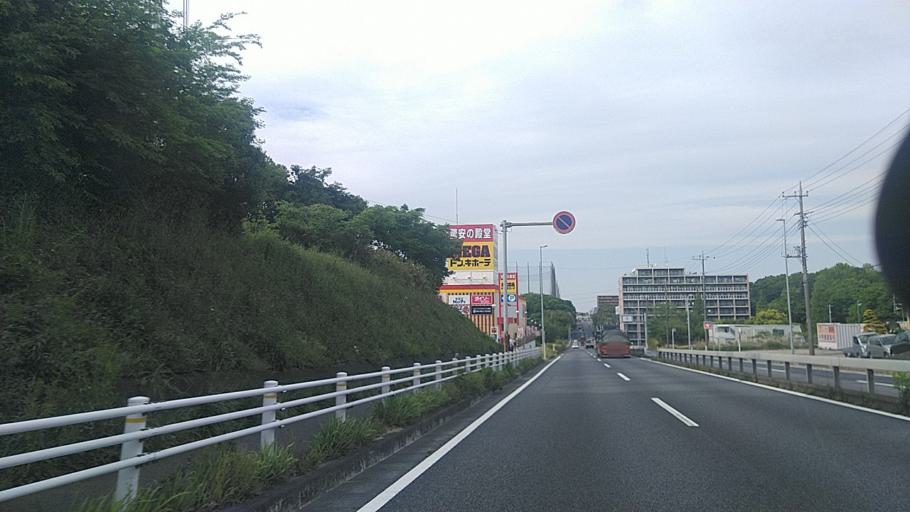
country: JP
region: Chiba
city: Shiroi
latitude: 35.7297
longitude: 140.1186
